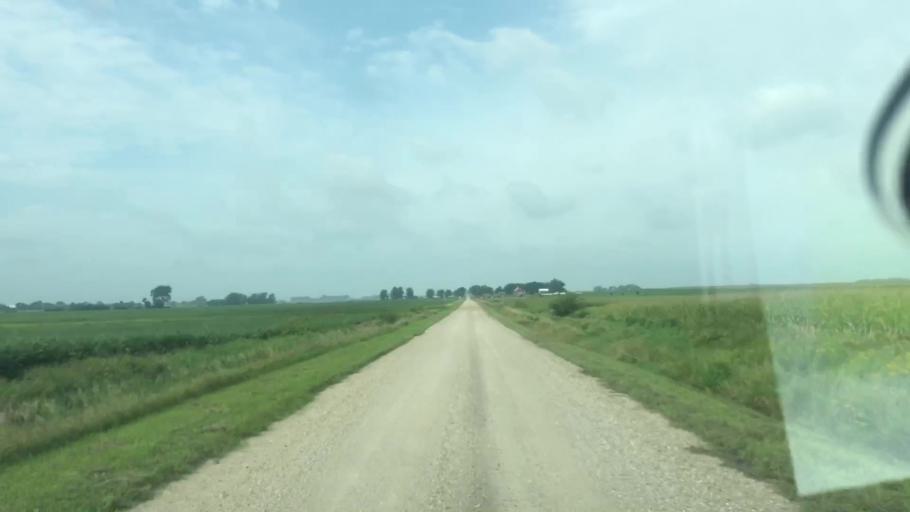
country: US
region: Iowa
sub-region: O'Brien County
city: Sheldon
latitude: 43.2725
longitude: -95.9039
